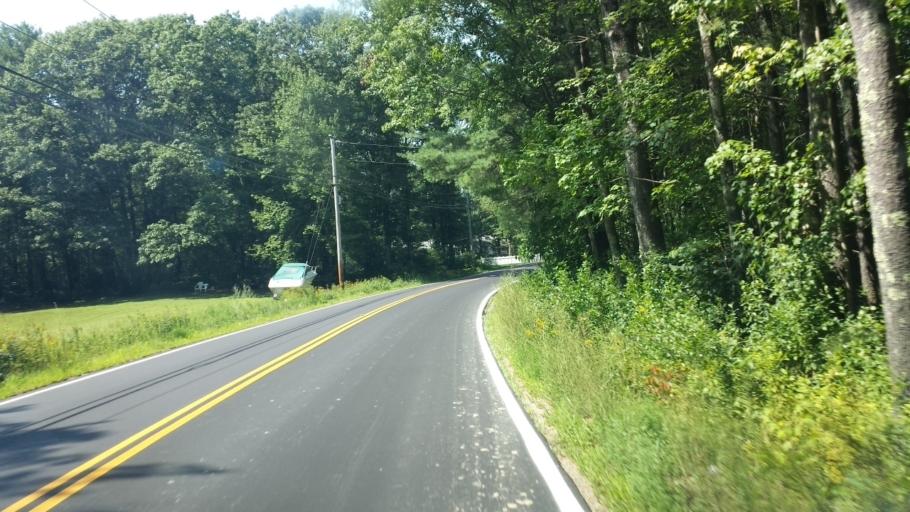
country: US
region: Maine
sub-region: York County
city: Arundel
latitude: 43.4132
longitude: -70.4983
